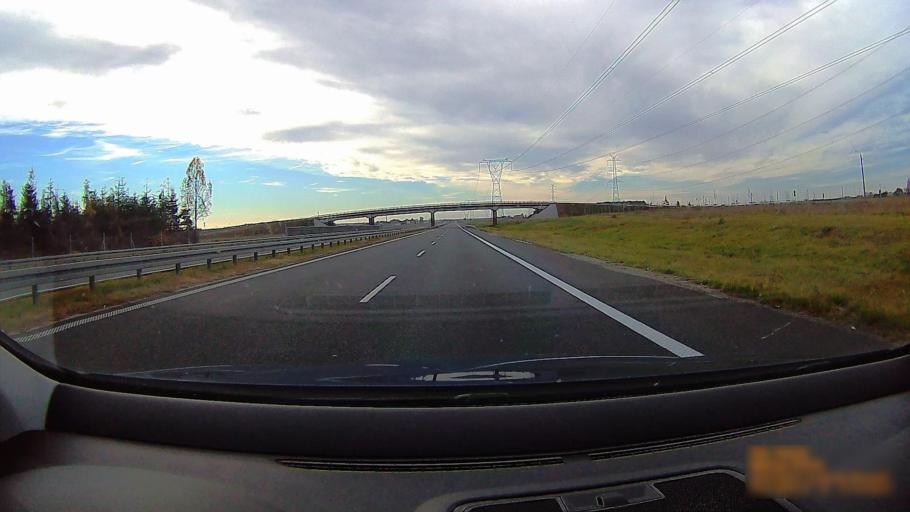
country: PL
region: Greater Poland Voivodeship
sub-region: Powiat ostrowski
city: Przygodzice
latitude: 51.6156
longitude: 17.8599
